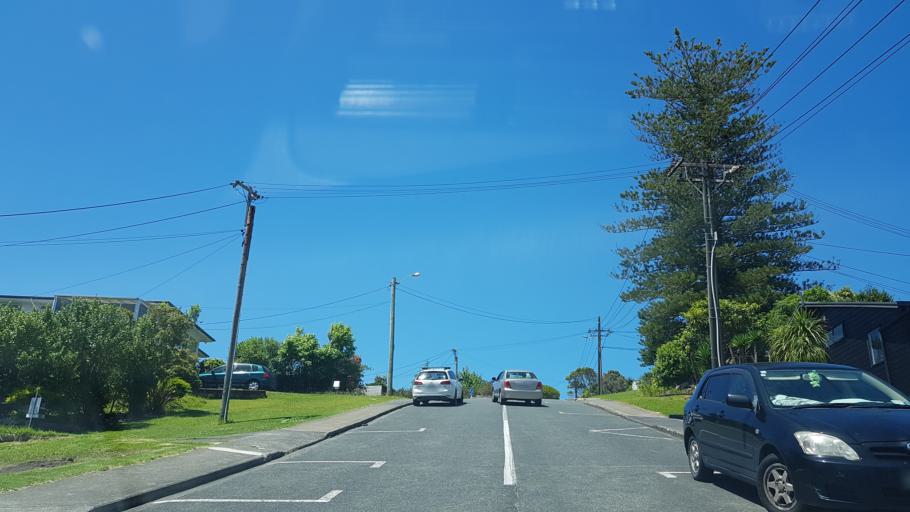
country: NZ
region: Auckland
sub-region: Auckland
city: North Shore
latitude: -36.8090
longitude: 174.7405
